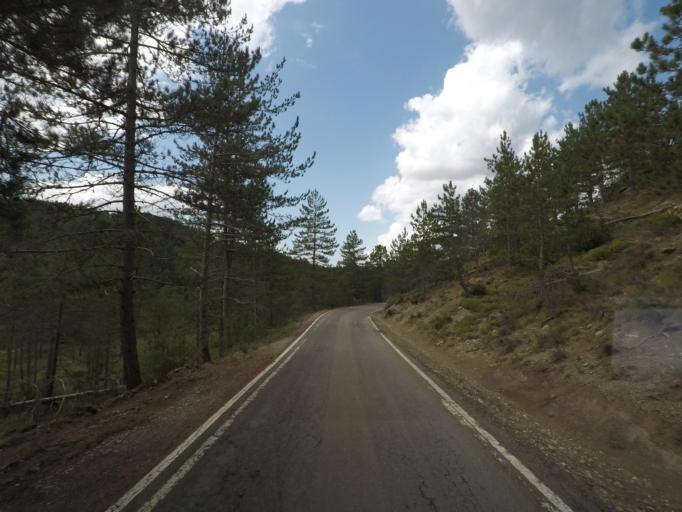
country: ES
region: Aragon
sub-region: Provincia de Huesca
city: Fiscal
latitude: 42.4068
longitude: -0.1475
